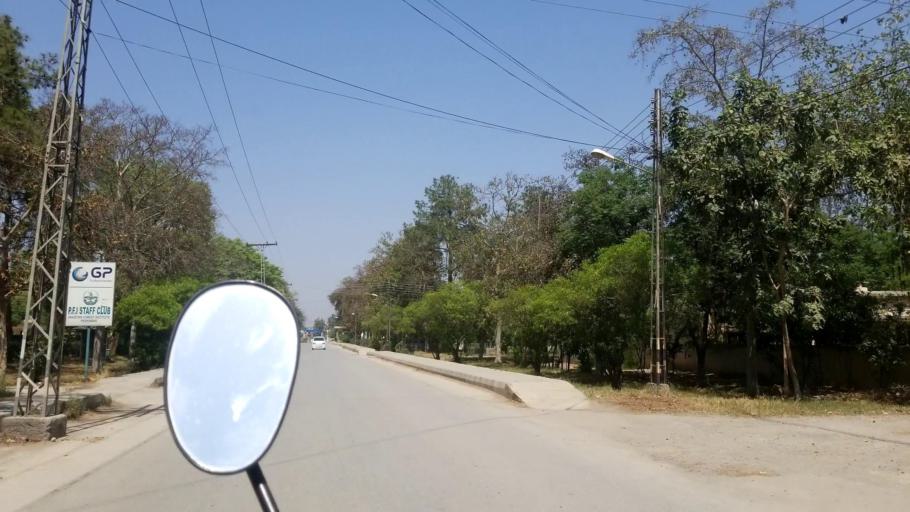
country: PK
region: Khyber Pakhtunkhwa
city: Peshawar
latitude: 34.0163
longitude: 71.4836
